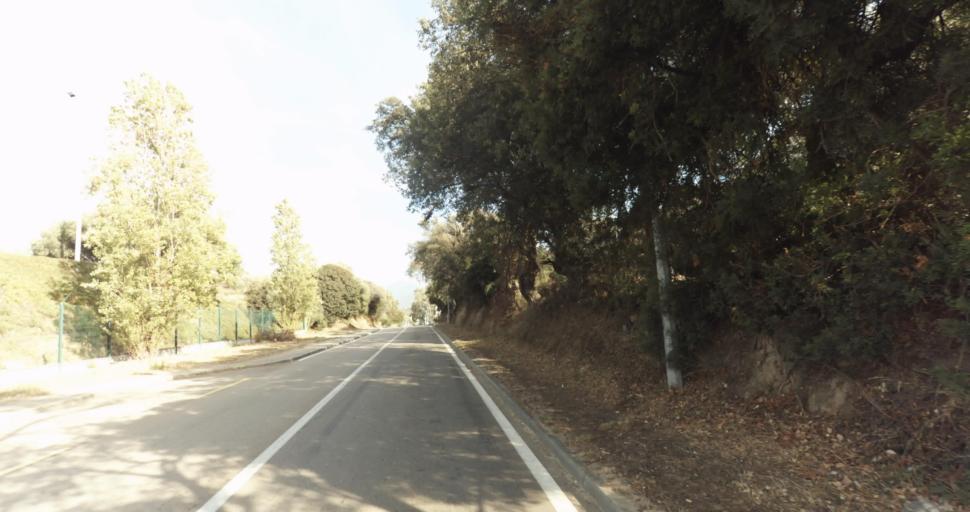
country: FR
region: Corsica
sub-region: Departement de la Corse-du-Sud
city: Afa
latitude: 41.9288
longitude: 8.7925
